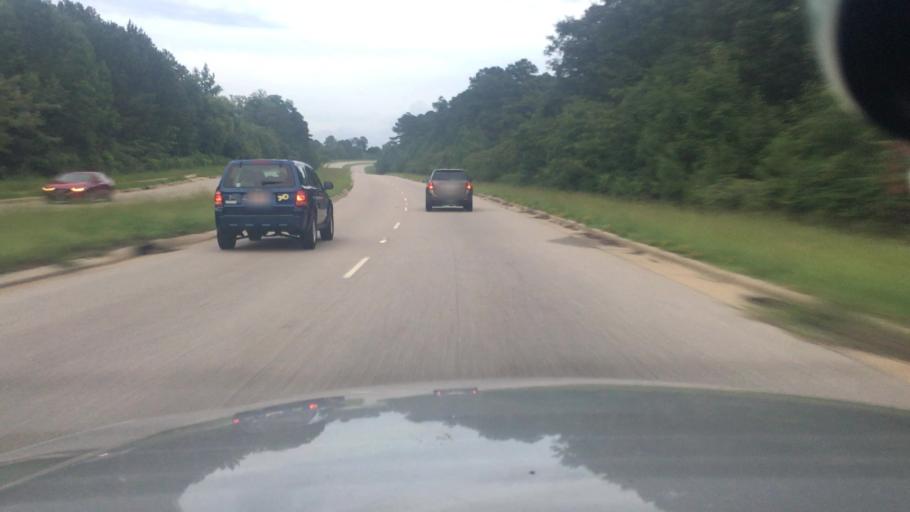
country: US
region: North Carolina
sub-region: Cumberland County
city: Hope Mills
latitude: 34.9910
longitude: -78.9583
